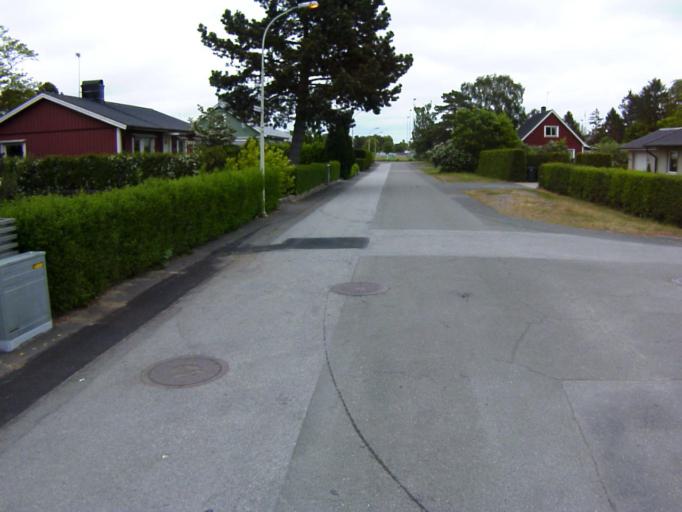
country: SE
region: Skane
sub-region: Kristianstads Kommun
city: Ahus
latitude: 55.9305
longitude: 14.2965
